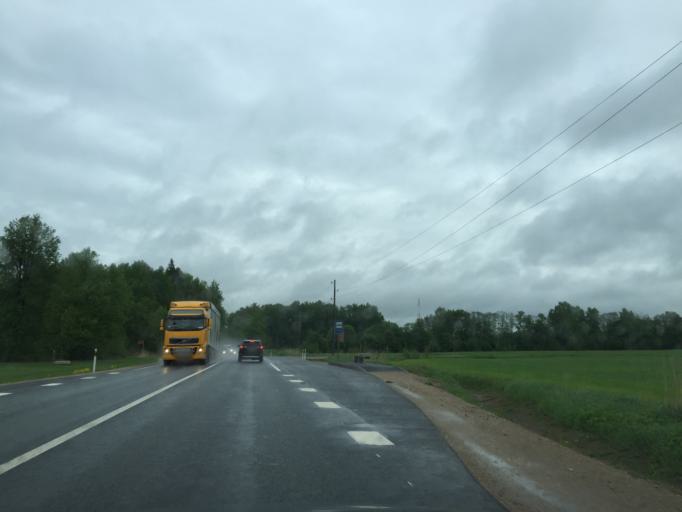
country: LV
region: Ogre
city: Jumprava
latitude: 56.6830
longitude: 24.8975
